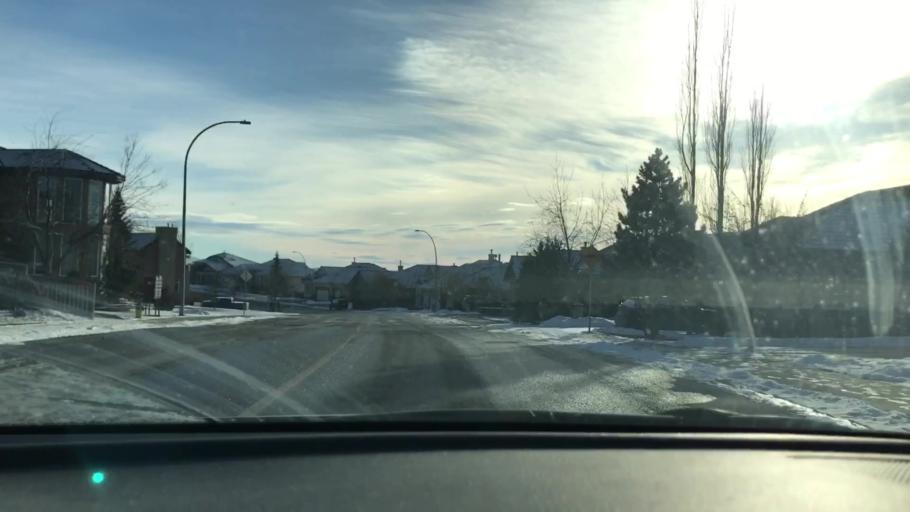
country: CA
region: Alberta
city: Calgary
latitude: 51.0236
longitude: -114.1772
